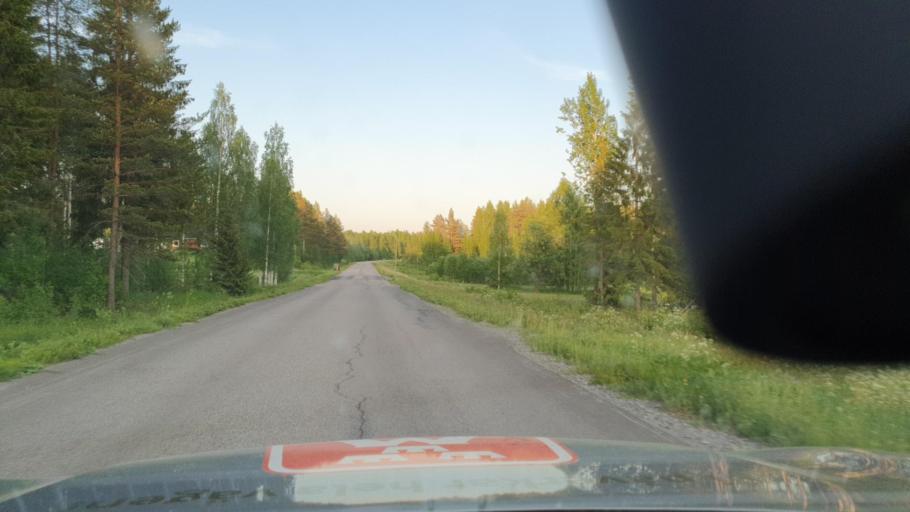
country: SE
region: Norrbotten
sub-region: Bodens Kommun
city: Boden
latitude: 66.0446
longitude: 21.7927
